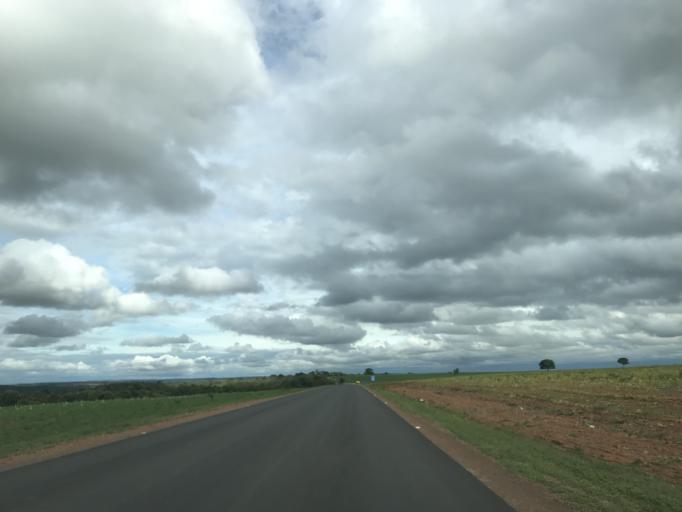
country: BR
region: Goias
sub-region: Vianopolis
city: Vianopolis
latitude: -16.9672
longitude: -48.6099
